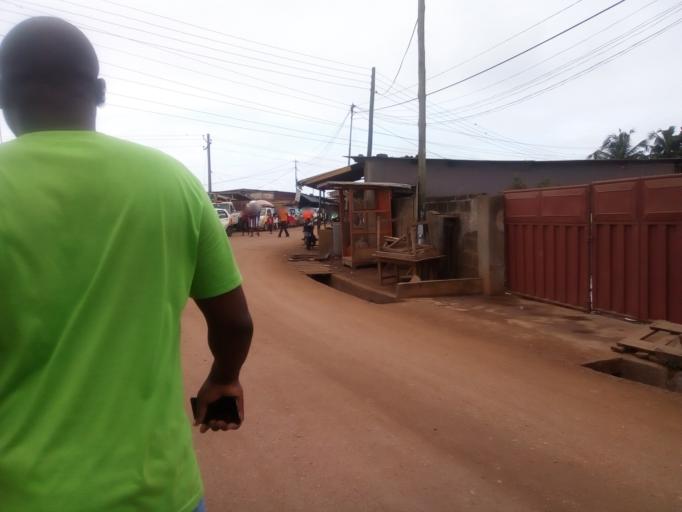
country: GH
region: Greater Accra
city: Dome
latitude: 5.6095
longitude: -0.2564
